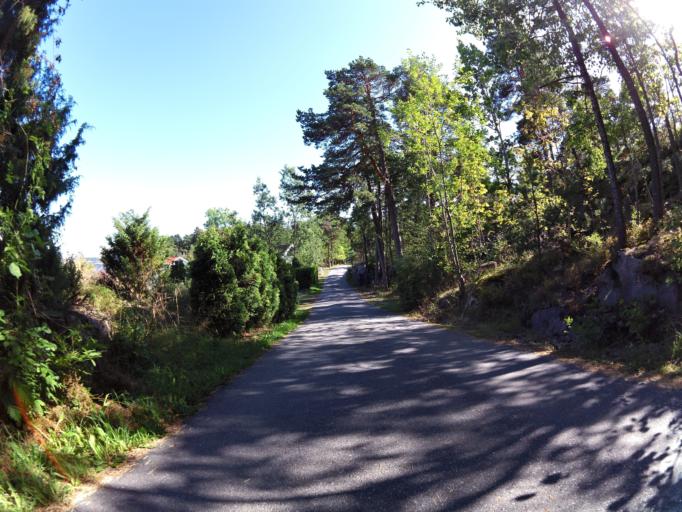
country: NO
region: Ostfold
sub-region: Fredrikstad
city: Fredrikstad
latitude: 59.1705
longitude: 10.8436
